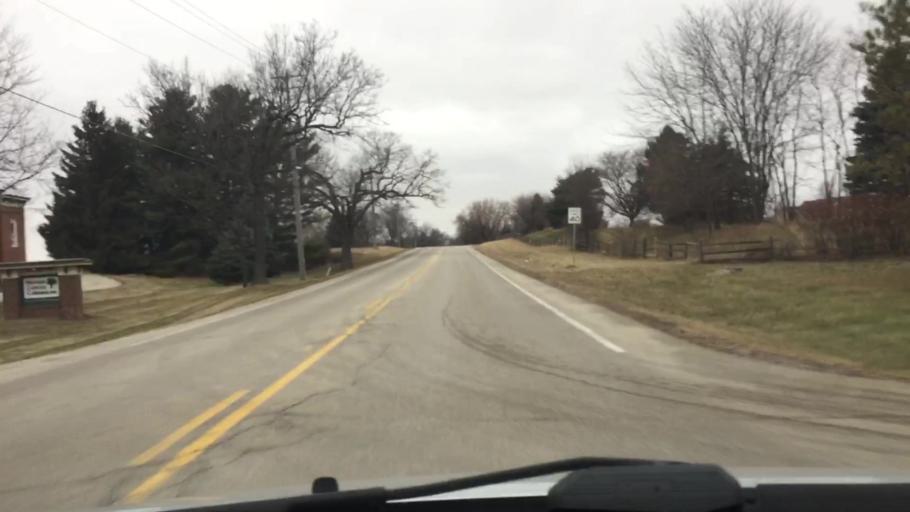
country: US
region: Wisconsin
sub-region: Waukesha County
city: Nashotah
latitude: 43.0839
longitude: -88.4033
